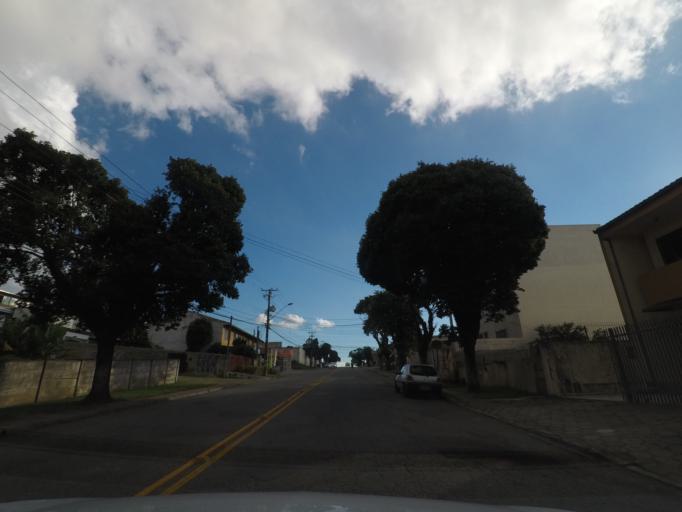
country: BR
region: Parana
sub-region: Sao Jose Dos Pinhais
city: Sao Jose dos Pinhais
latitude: -25.5045
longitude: -49.2623
